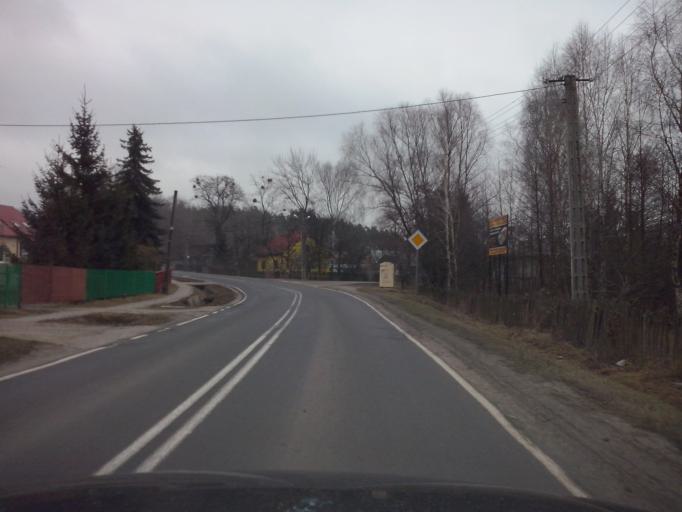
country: PL
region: Subcarpathian Voivodeship
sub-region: Powiat nizanski
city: Zarzecze
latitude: 50.5175
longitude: 22.2135
